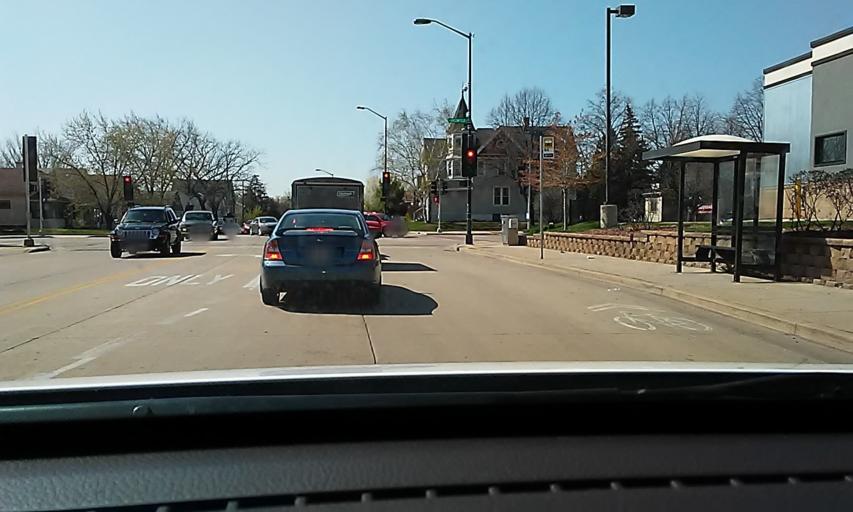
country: US
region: Wisconsin
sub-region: Milwaukee County
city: West Milwaukee
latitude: 43.0172
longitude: -87.9875
